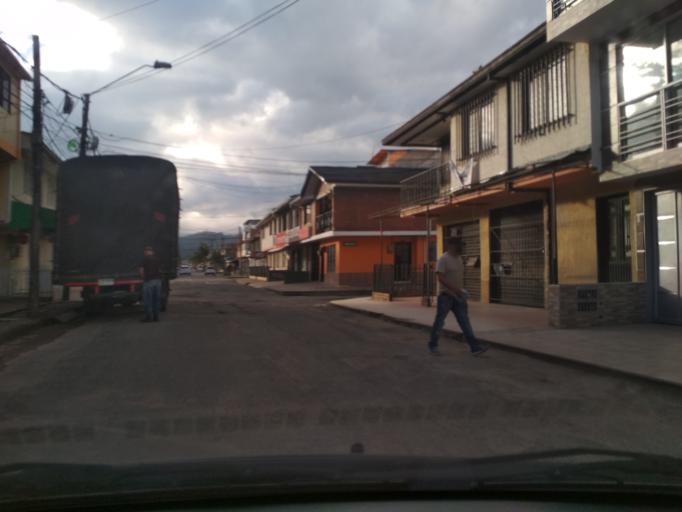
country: CO
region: Cauca
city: Popayan
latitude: 2.4424
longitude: -76.6148
